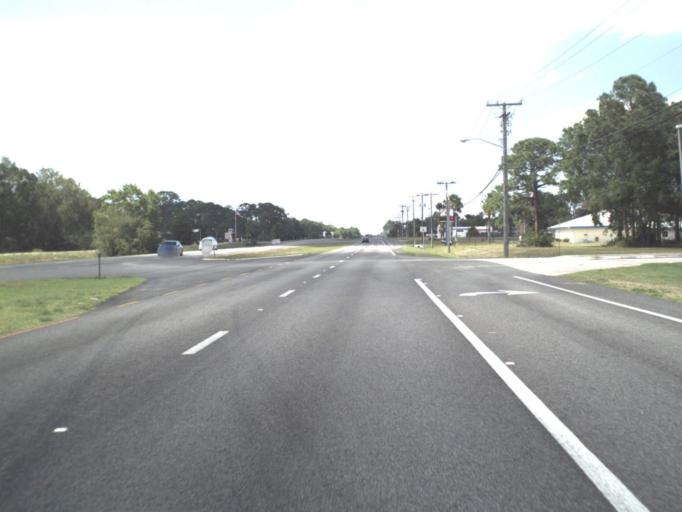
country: US
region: Florida
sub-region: Brevard County
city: Titusville
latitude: 28.6315
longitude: -80.8263
